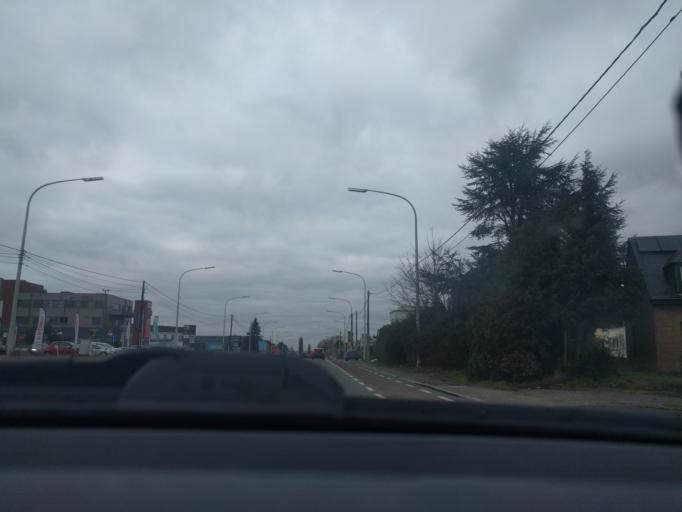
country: BE
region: Wallonia
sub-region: Province de Namur
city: Namur
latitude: 50.4410
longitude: 4.9065
